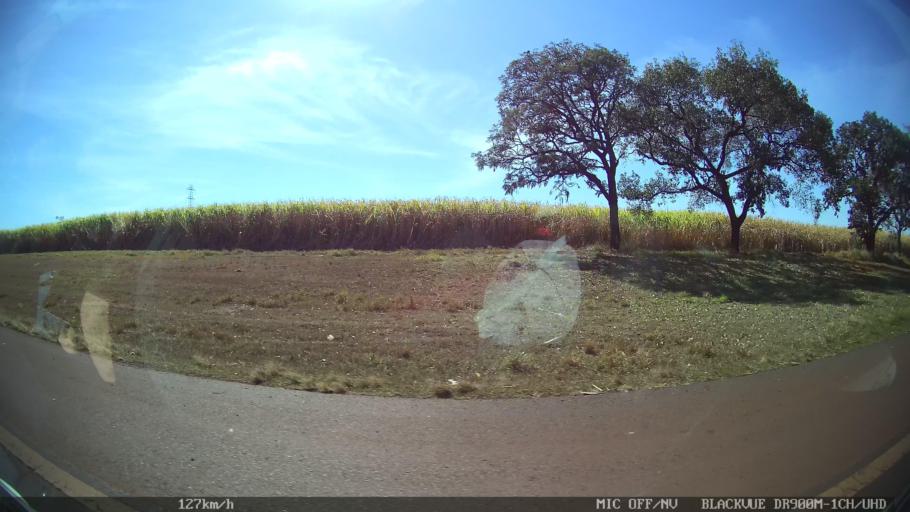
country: BR
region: Sao Paulo
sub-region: Ipua
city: Ipua
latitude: -20.4503
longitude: -48.1791
